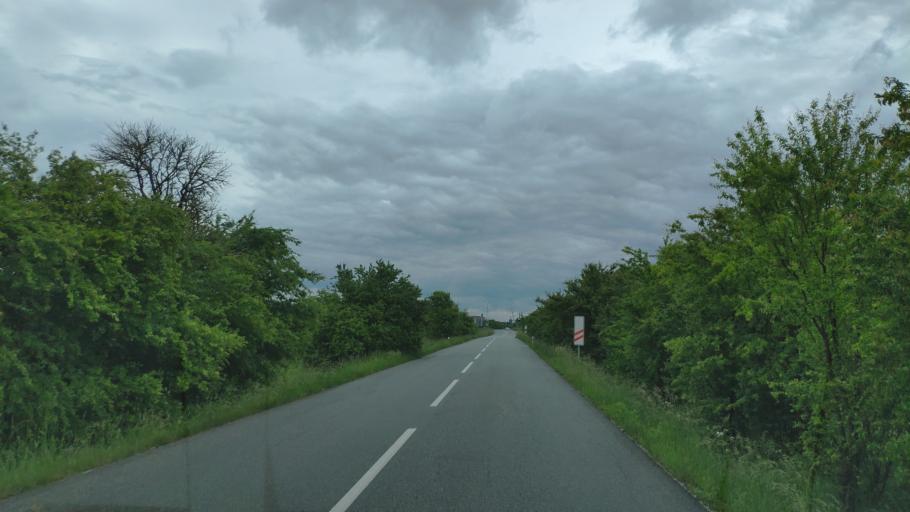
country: SK
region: Kosicky
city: Moldava nad Bodvou
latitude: 48.5853
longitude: 21.1410
